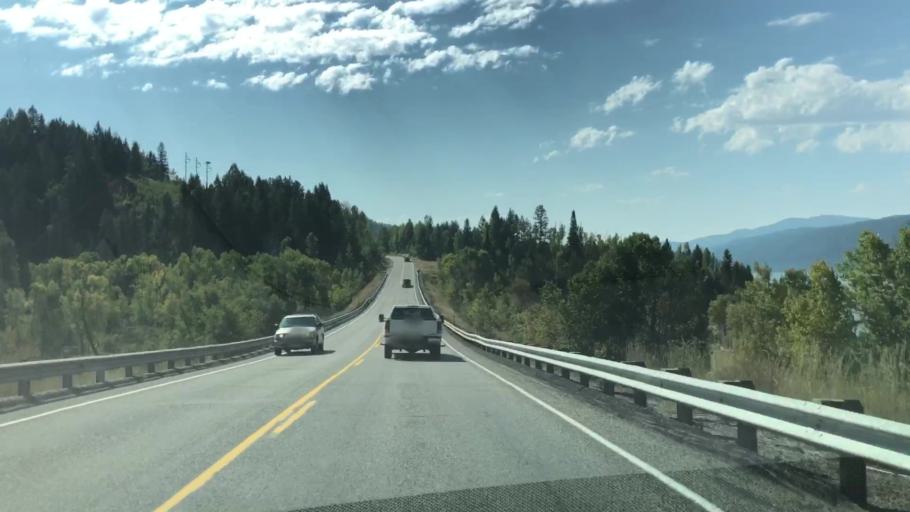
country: US
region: Idaho
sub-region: Teton County
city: Victor
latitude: 43.2846
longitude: -111.1203
